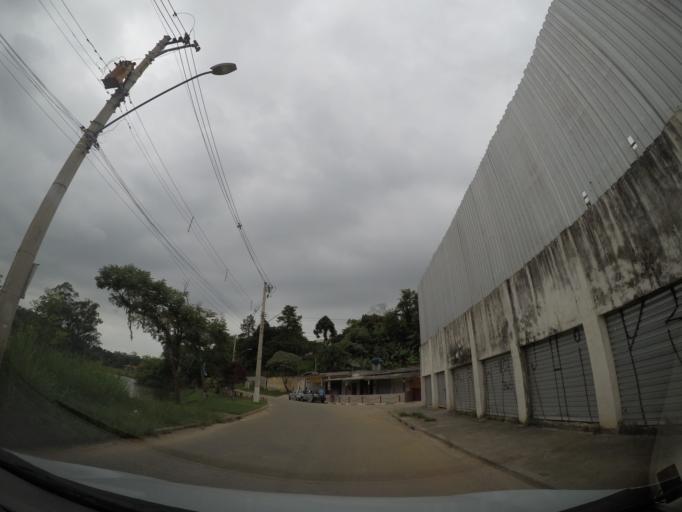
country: BR
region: Sao Paulo
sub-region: Aruja
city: Aruja
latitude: -23.3614
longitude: -46.4056
